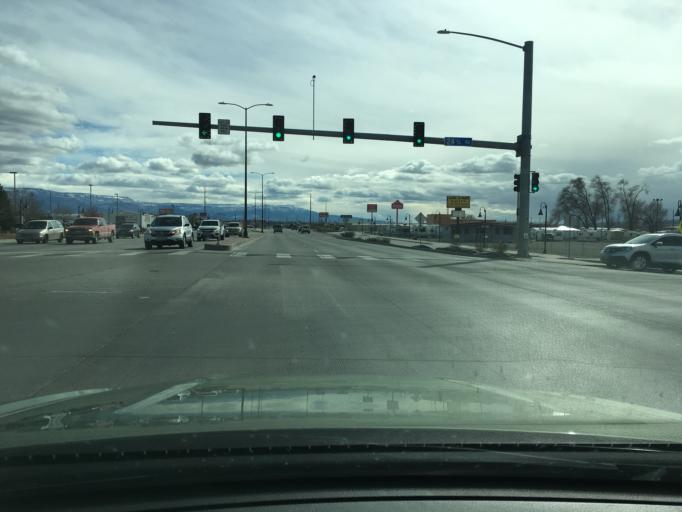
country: US
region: Colorado
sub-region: Mesa County
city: Redlands
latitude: 39.0850
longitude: -108.5942
